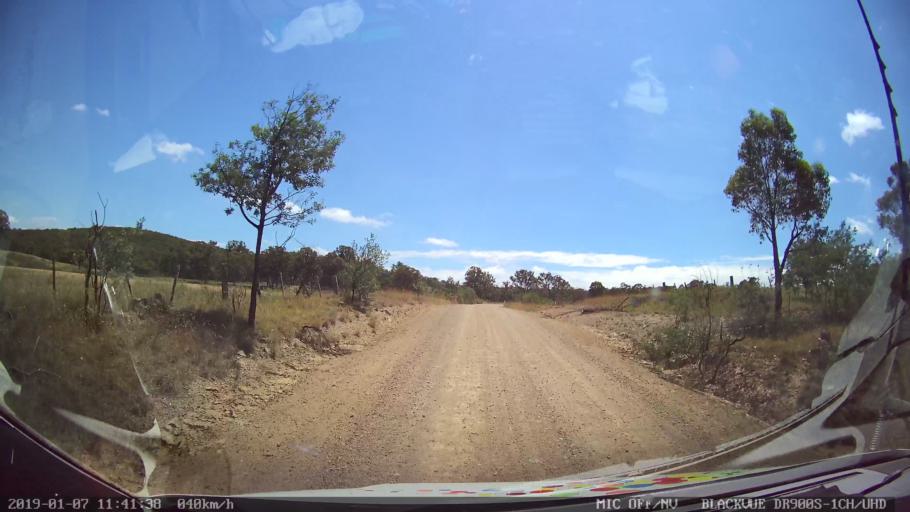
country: AU
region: New South Wales
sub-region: Guyra
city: Guyra
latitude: -30.3596
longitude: 151.5893
